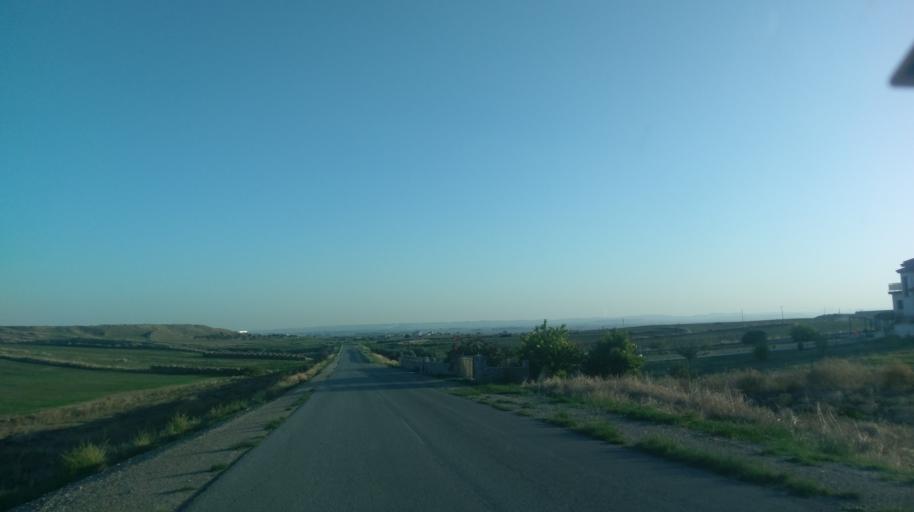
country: CY
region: Ammochostos
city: Lefkonoiko
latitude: 35.2525
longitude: 33.5497
